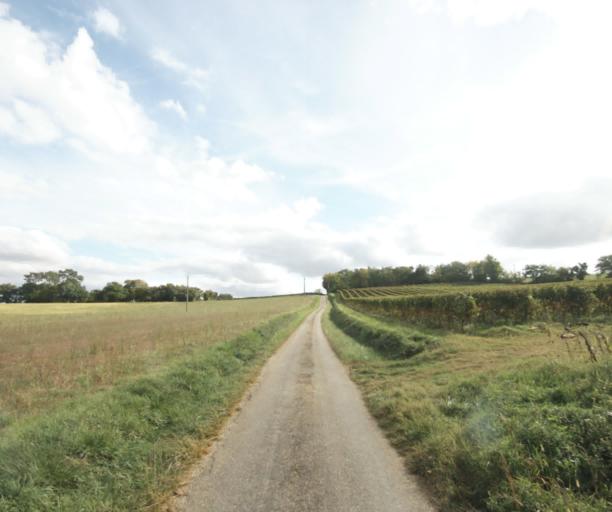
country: FR
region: Midi-Pyrenees
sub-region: Departement du Gers
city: Gondrin
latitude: 43.8573
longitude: 0.2719
